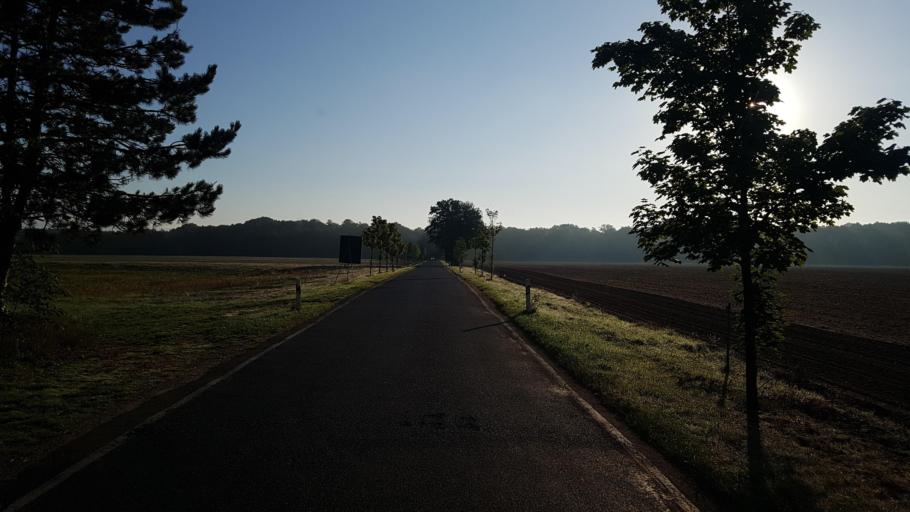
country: DE
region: Saxony-Anhalt
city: Holzdorf
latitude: 51.8274
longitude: 13.0767
